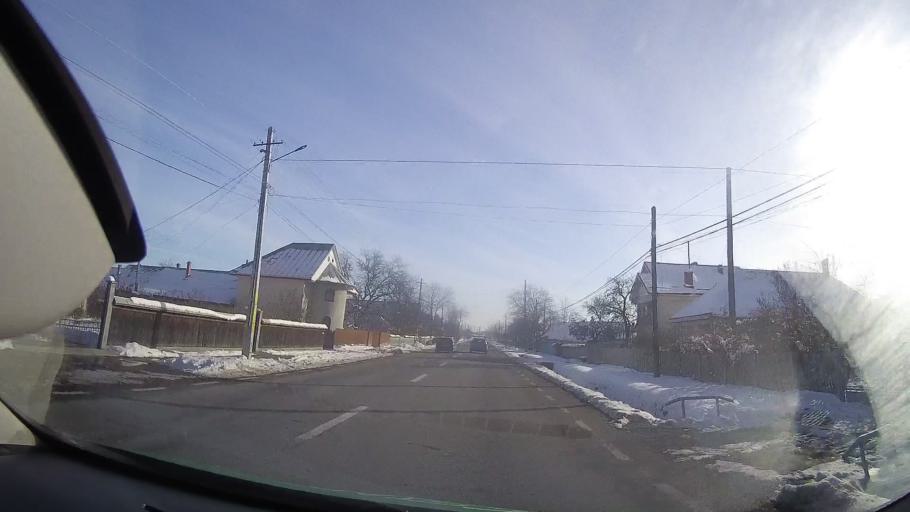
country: RO
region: Neamt
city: Bodesti
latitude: 47.0341
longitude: 26.4133
